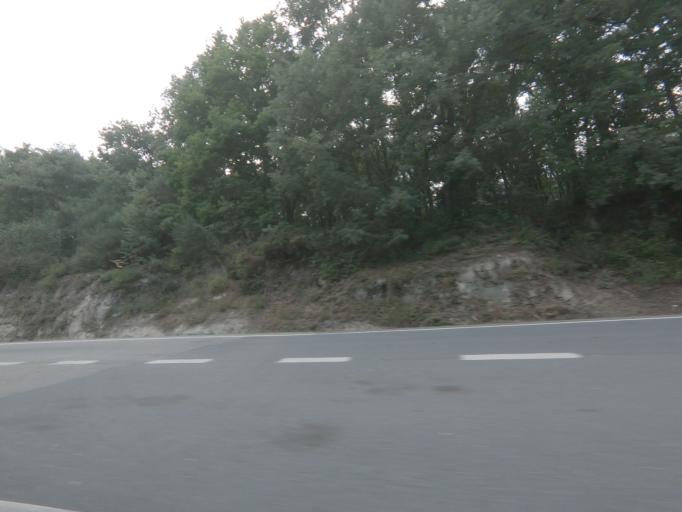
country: ES
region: Galicia
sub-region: Provincia de Ourense
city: Taboadela
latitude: 42.2405
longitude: -7.8449
